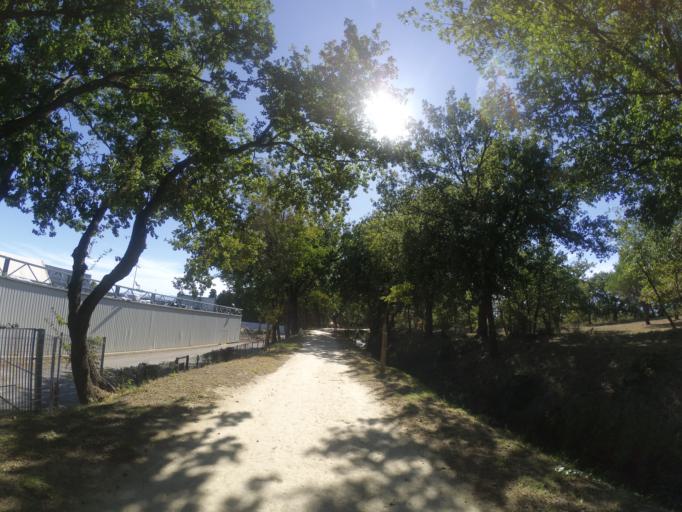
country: FR
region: Languedoc-Roussillon
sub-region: Departement des Pyrenees-Orientales
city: Perpignan
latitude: 42.6803
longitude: 2.8892
